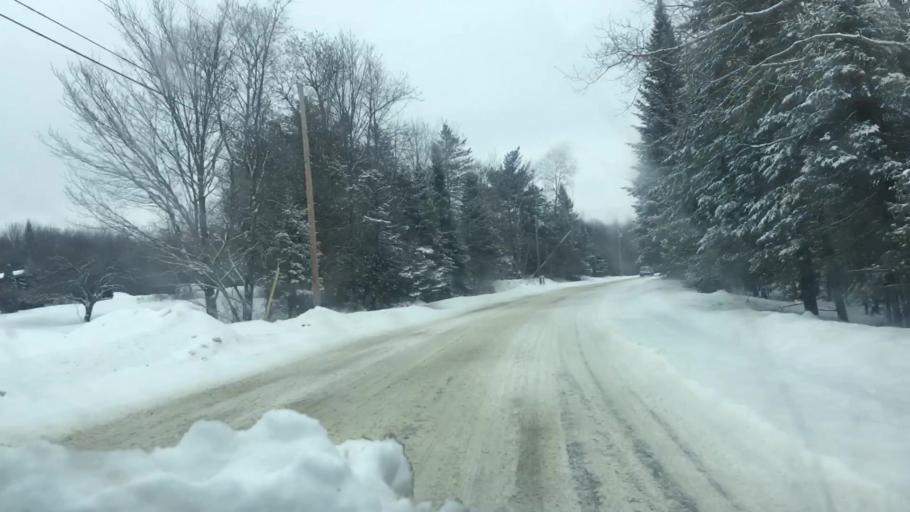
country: US
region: Maine
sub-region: Penobscot County
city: Bradford
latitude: 45.0322
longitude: -68.9492
